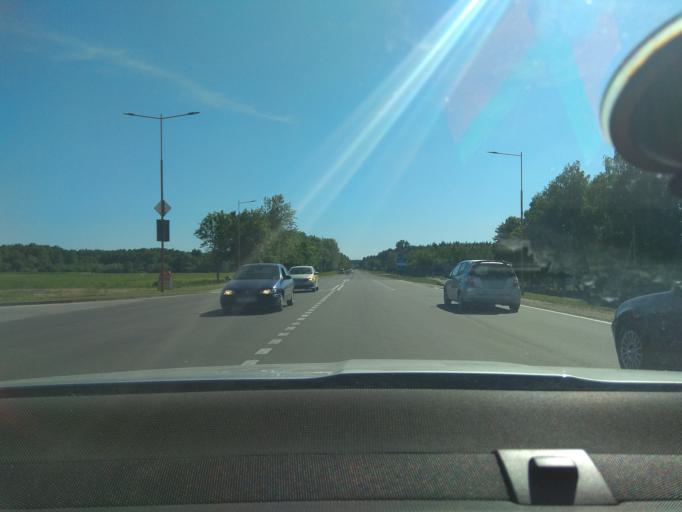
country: BY
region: Grodnenskaya
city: Hrodna
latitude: 53.6452
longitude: 23.7753
